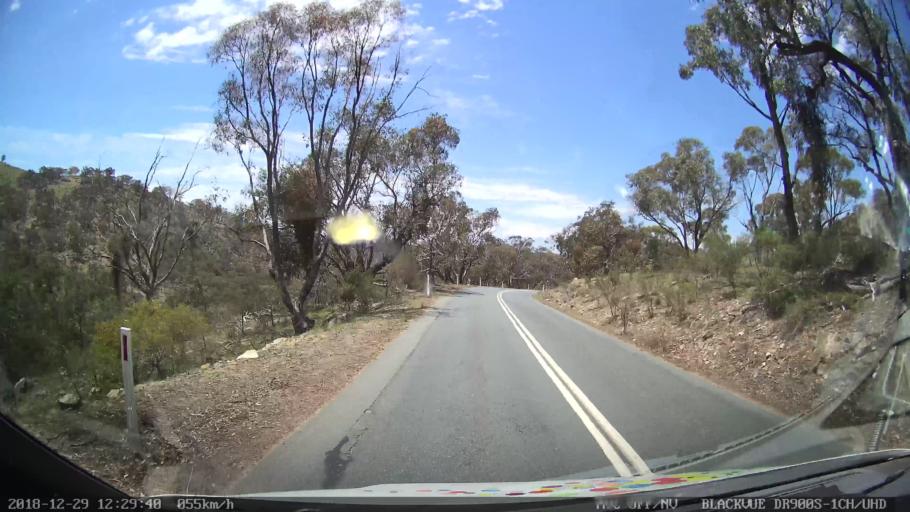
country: AU
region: Australian Capital Territory
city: Macarthur
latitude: -35.5000
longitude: 149.2310
